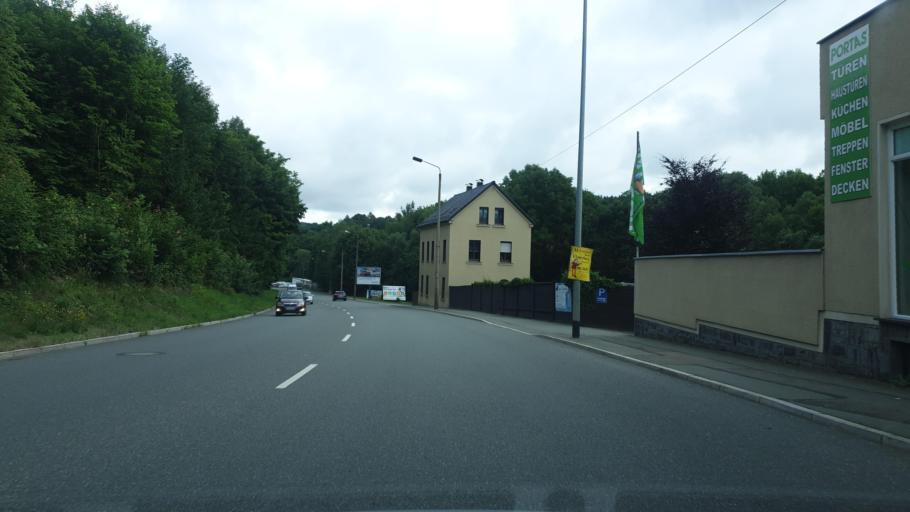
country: DE
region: Saxony
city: Netzschkau
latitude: 50.6152
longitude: 12.2533
